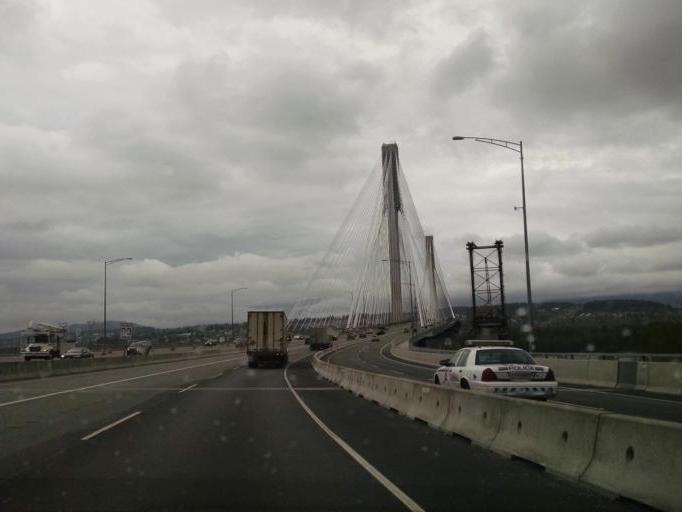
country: CA
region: British Columbia
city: Port Moody
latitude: 49.2119
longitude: -122.8093
